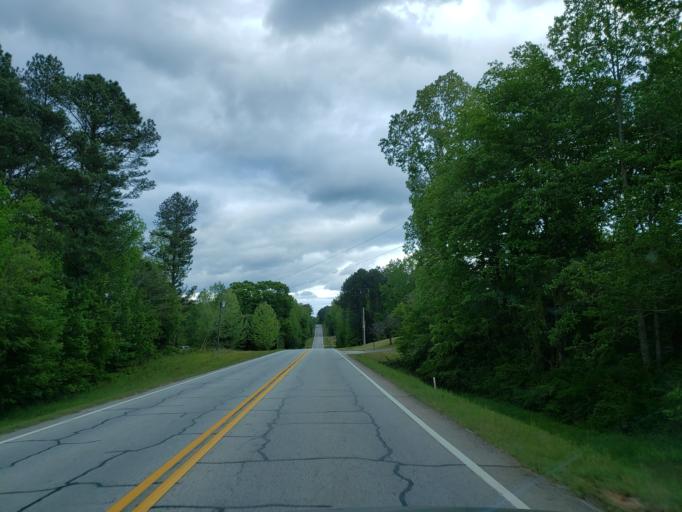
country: US
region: Georgia
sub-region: Haralson County
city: Buchanan
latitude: 33.8164
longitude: -85.1145
